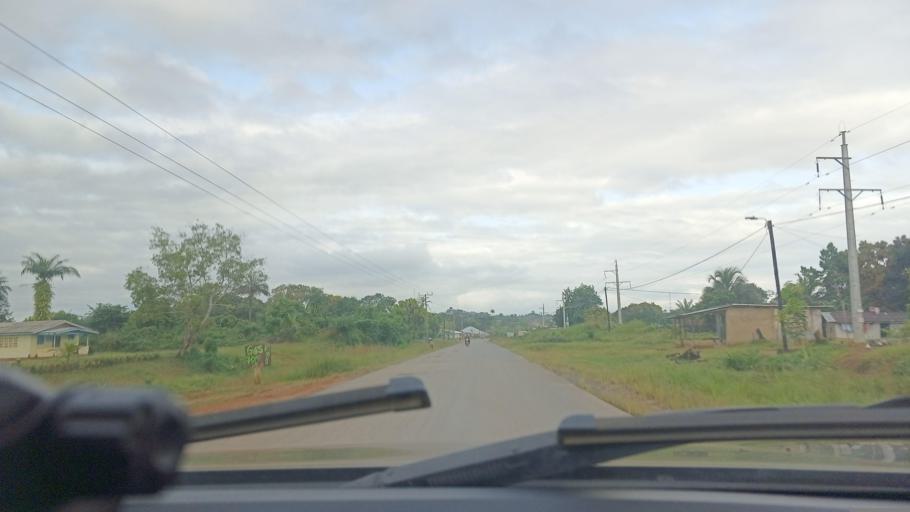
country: LR
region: Montserrado
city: Monrovia
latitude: 6.5711
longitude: -10.8792
